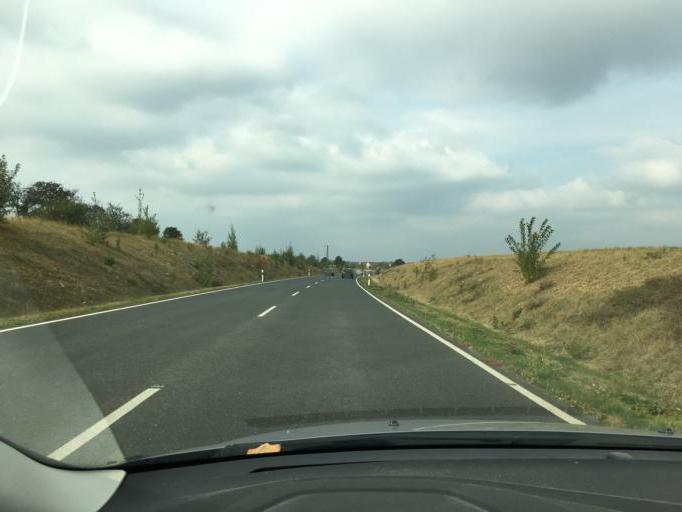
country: DE
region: Saxony
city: Bannewitz
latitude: 50.9877
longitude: 13.7286
